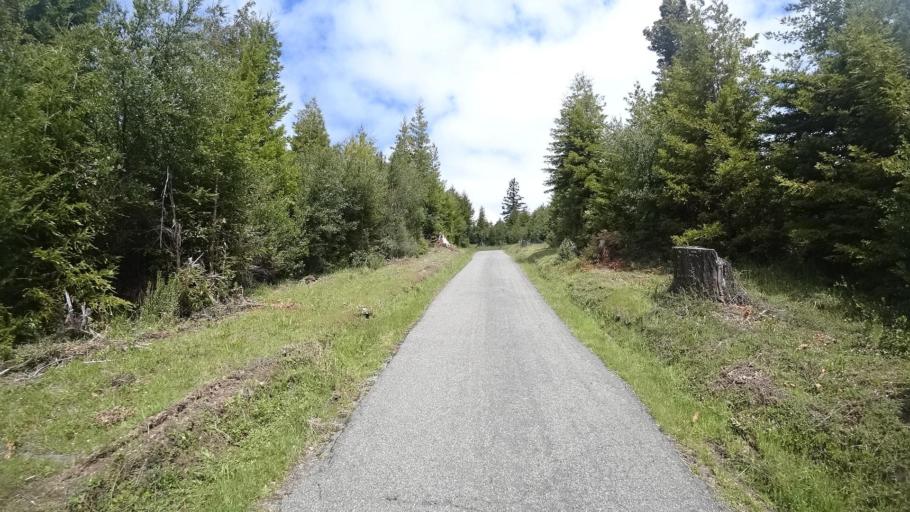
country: US
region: California
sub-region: Humboldt County
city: Blue Lake
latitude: 40.7869
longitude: -123.9658
